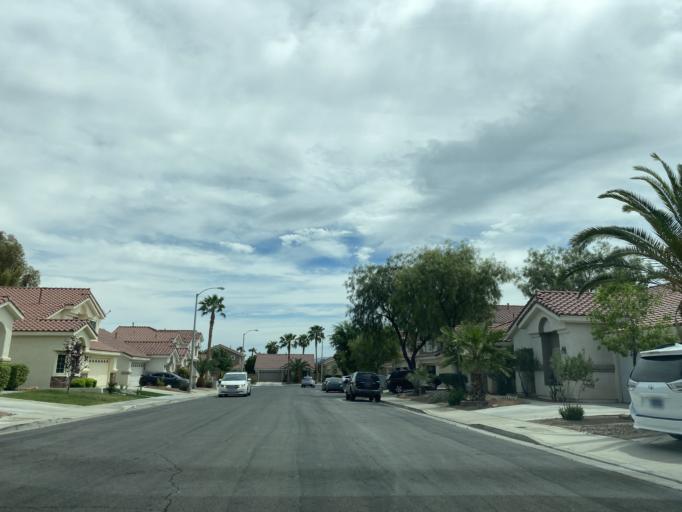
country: US
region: Nevada
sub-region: Clark County
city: Whitney
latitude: 36.0250
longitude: -115.0689
